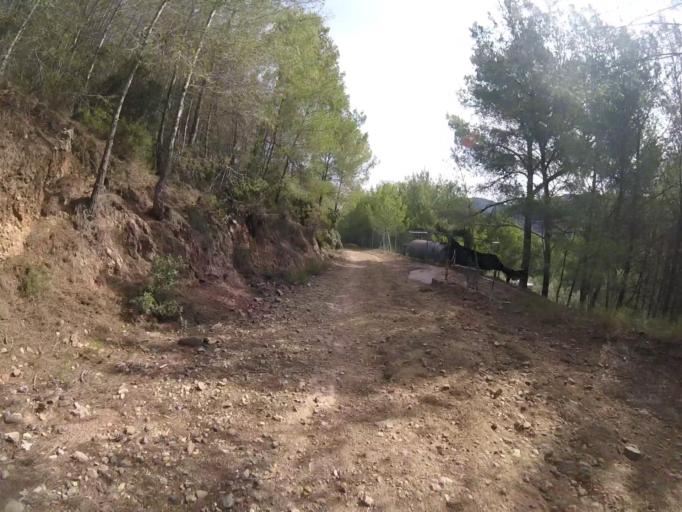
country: ES
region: Valencia
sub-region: Provincia de Castello
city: Benicassim
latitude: 40.0846
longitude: 0.0527
